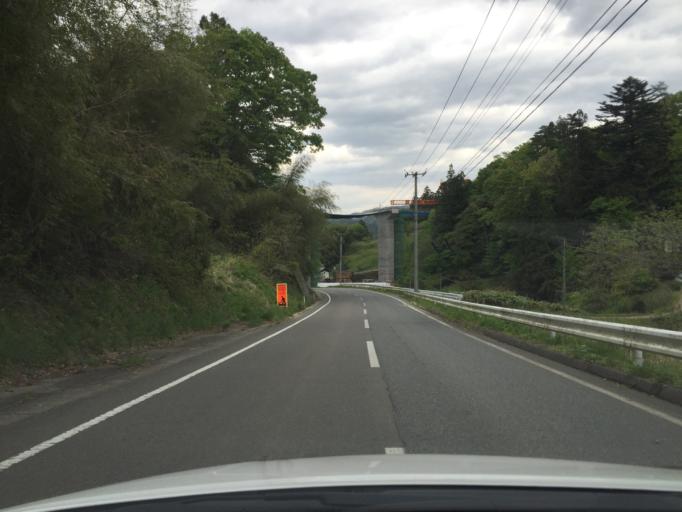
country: JP
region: Fukushima
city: Yanagawamachi-saiwaicho
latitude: 37.7453
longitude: 140.6390
